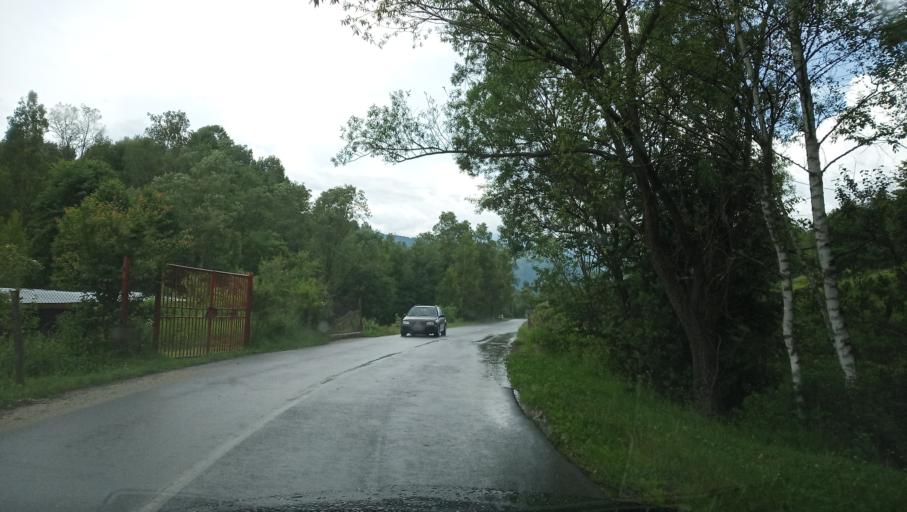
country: RO
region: Hunedoara
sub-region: Oras Petrila
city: Petrila
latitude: 45.4054
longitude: 23.4121
